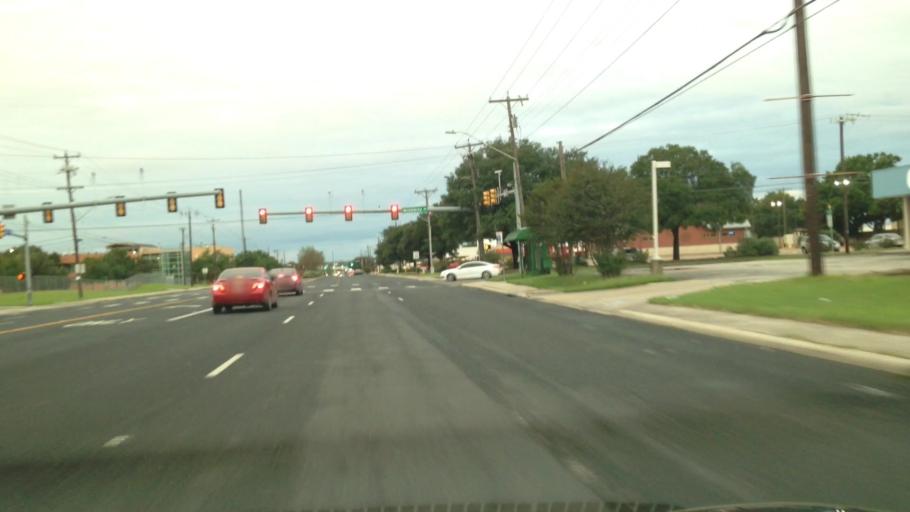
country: US
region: Texas
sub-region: Bexar County
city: Windcrest
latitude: 29.5104
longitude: -98.3872
